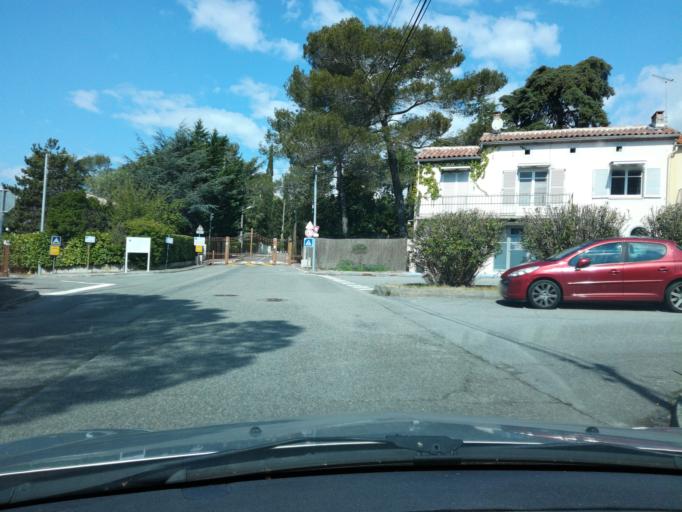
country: FR
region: Provence-Alpes-Cote d'Azur
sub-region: Departement des Alpes-Maritimes
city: Mougins
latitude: 43.6033
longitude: 7.0211
